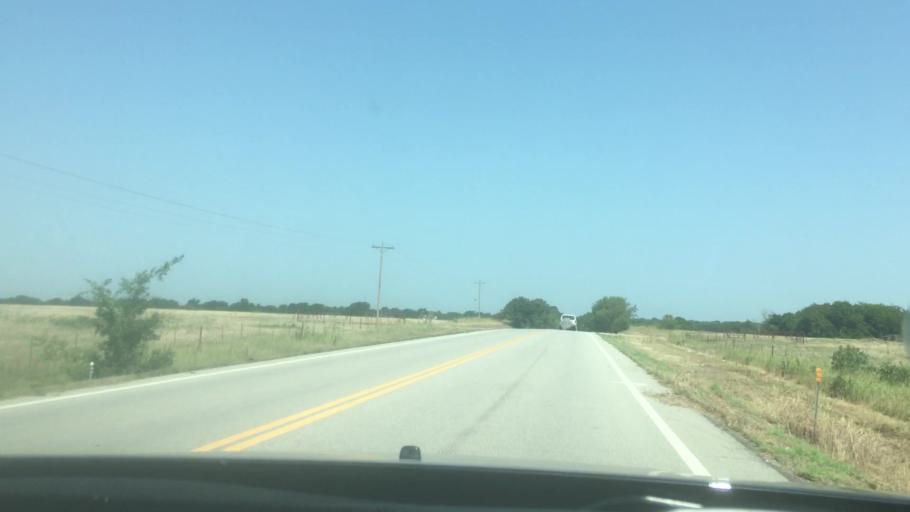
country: US
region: Oklahoma
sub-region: Bryan County
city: Durant
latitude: 34.1651
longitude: -96.4004
